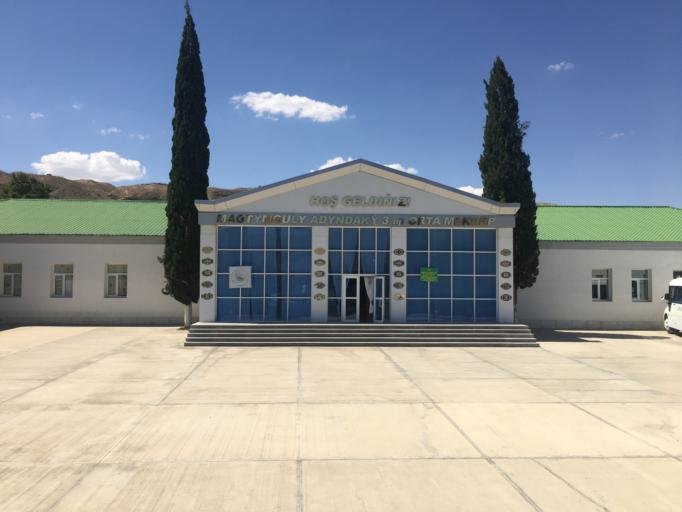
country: TM
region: Balkan
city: Magtymguly
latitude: 38.4455
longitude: 56.4998
